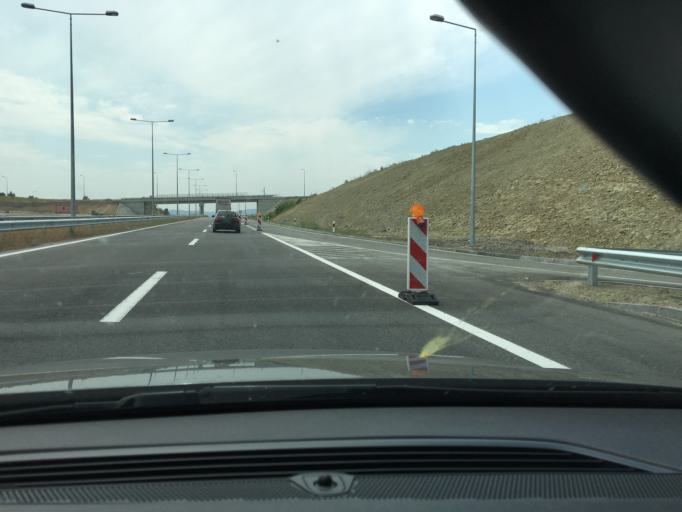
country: MK
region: Stip
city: Shtip
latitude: 41.7822
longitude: 22.1244
